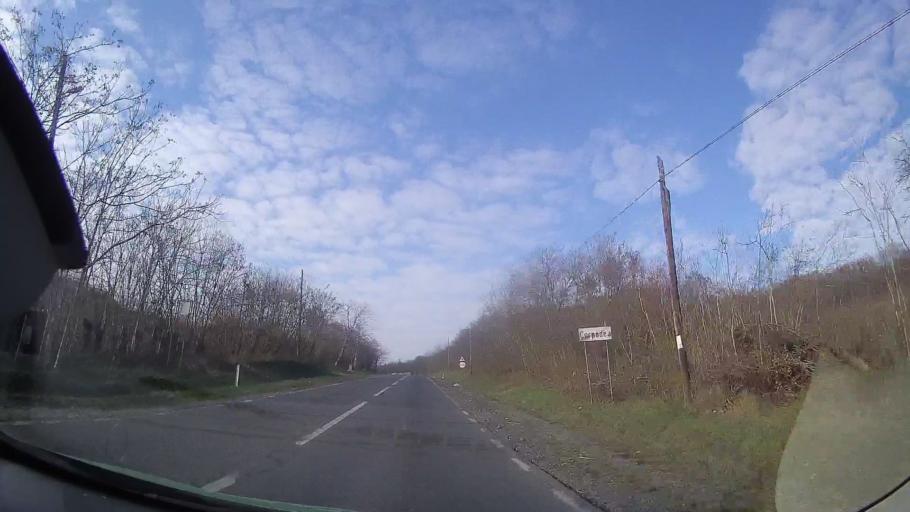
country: RO
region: Cluj
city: Jucu Herghelia
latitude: 46.8100
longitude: 23.8370
